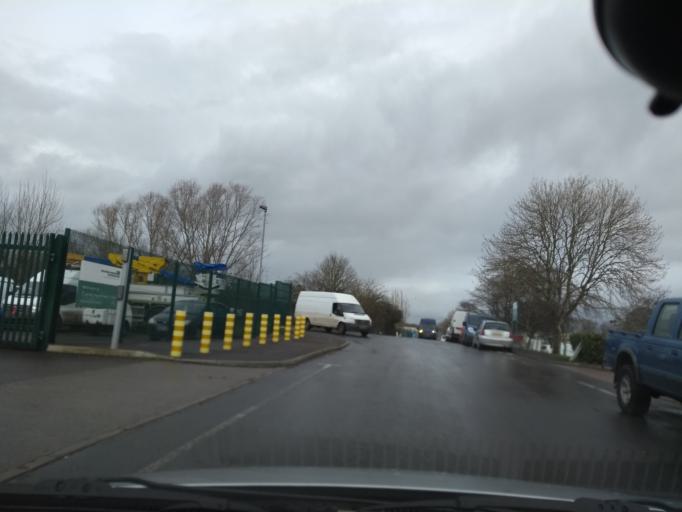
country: GB
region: England
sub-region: Somerset
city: Taunton
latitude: 51.0263
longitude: -3.0864
